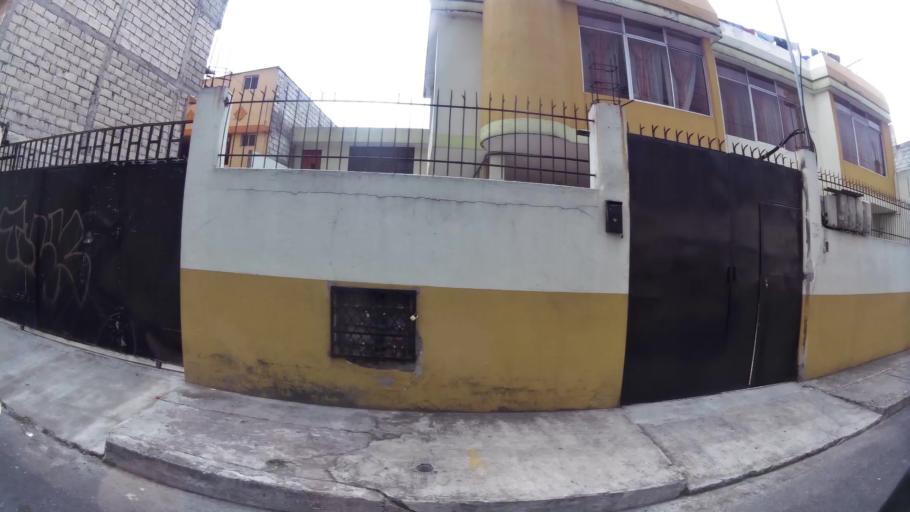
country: EC
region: Pichincha
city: Quito
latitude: -0.2864
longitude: -78.5395
